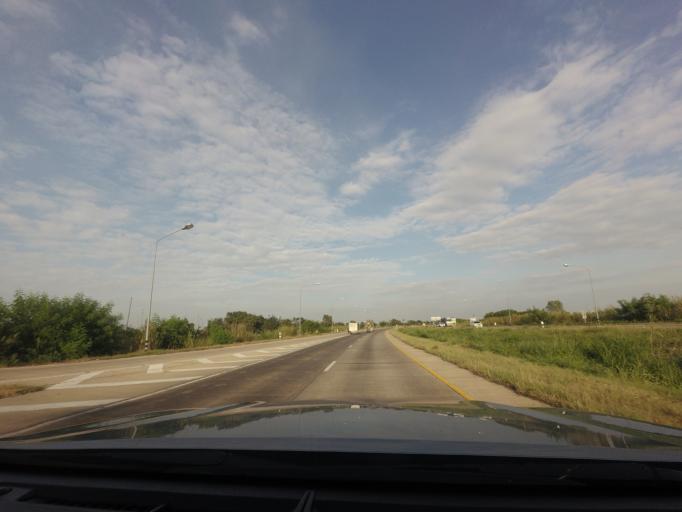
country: TH
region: Nakhon Sawan
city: Nakhon Sawan
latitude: 15.7670
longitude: 100.1050
